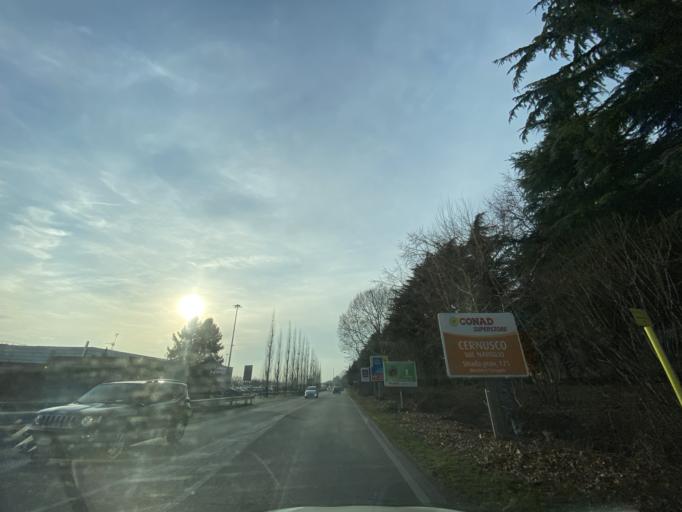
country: IT
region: Lombardy
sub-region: Citta metropolitana di Milano
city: Pioltello
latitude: 45.5146
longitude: 9.3255
